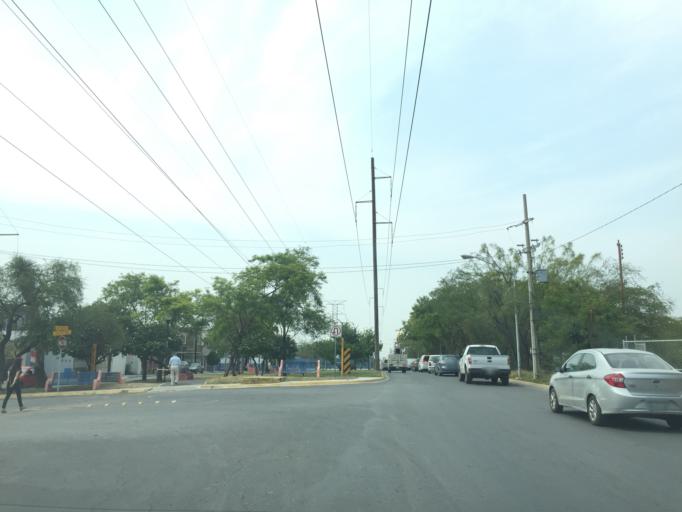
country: MX
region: Nuevo Leon
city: Guadalupe
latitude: 25.7203
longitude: -100.2213
